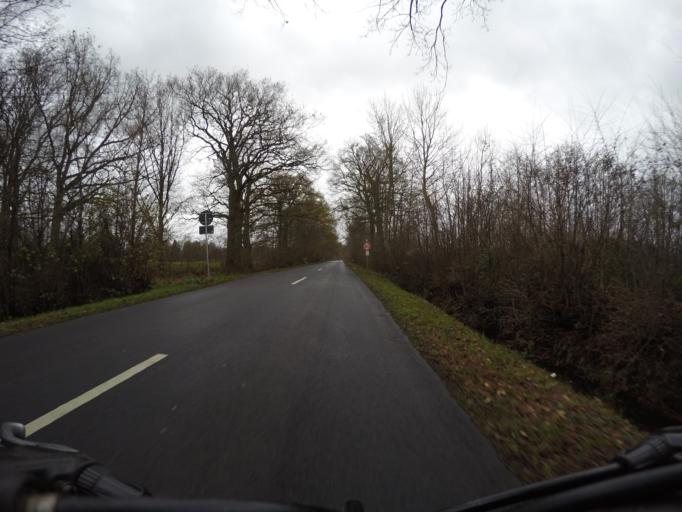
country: DE
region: Schleswig-Holstein
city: Hasloh
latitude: 53.7049
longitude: 9.8783
